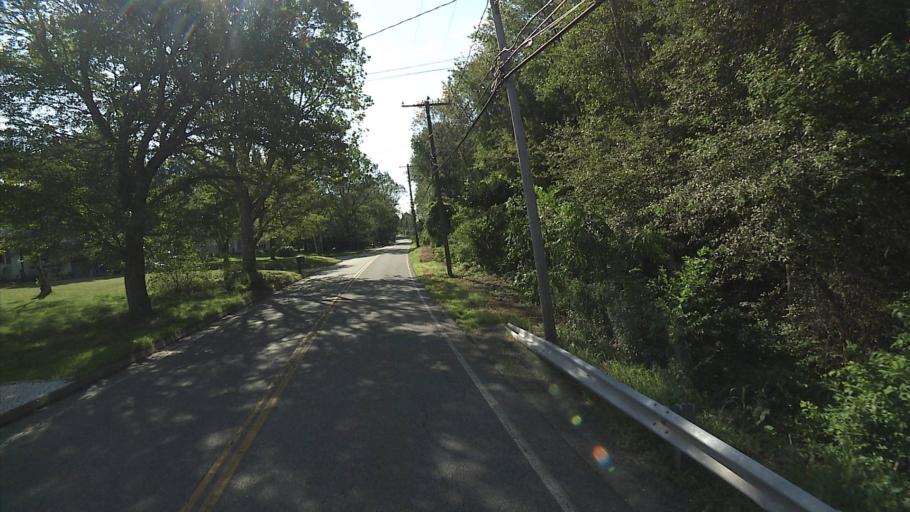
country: US
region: Connecticut
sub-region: New London County
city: Montville Center
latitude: 41.4944
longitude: -72.1827
